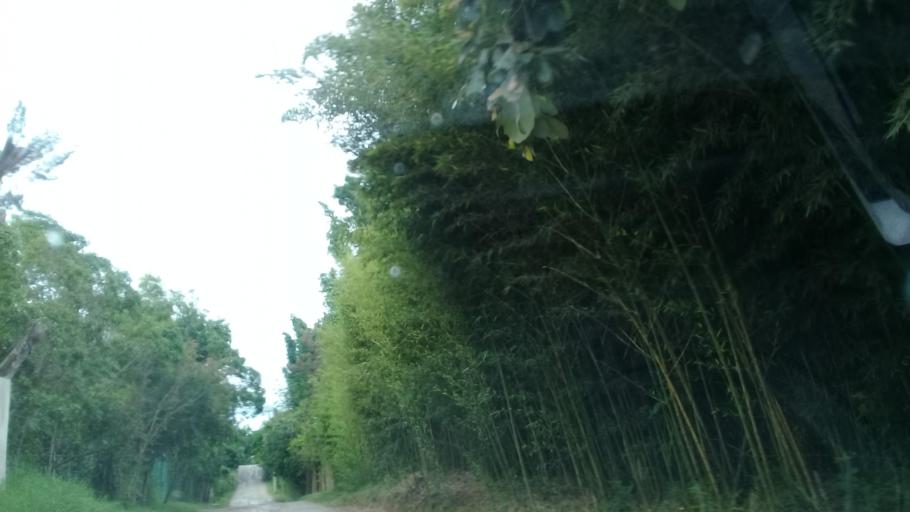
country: MX
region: Veracruz
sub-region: Emiliano Zapata
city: Jacarandas
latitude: 19.5059
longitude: -96.8433
